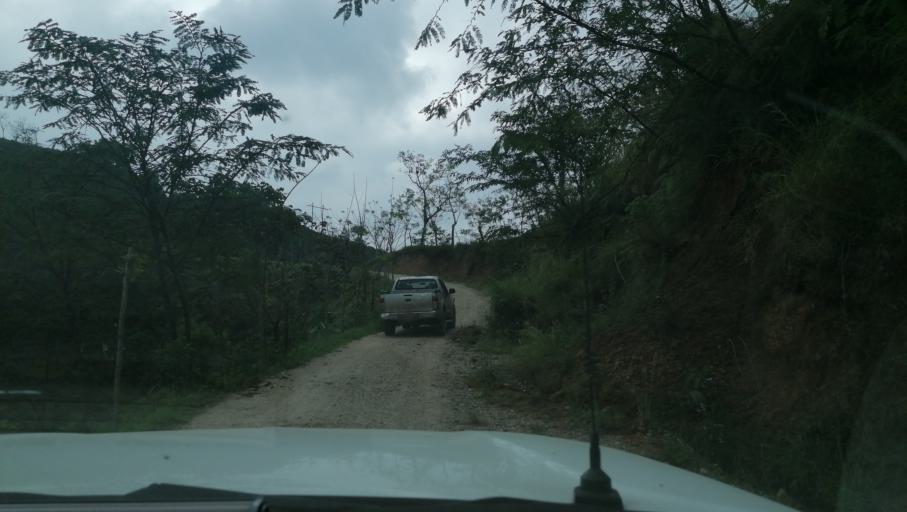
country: MX
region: Chiapas
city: Ostuacan
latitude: 17.3456
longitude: -93.3089
